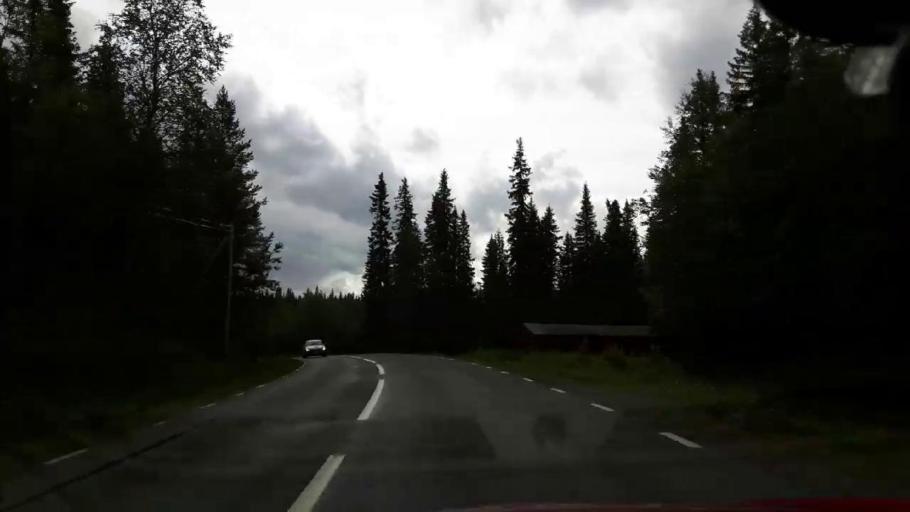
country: NO
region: Nord-Trondelag
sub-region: Lierne
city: Sandvika
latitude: 64.5113
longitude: 14.1559
